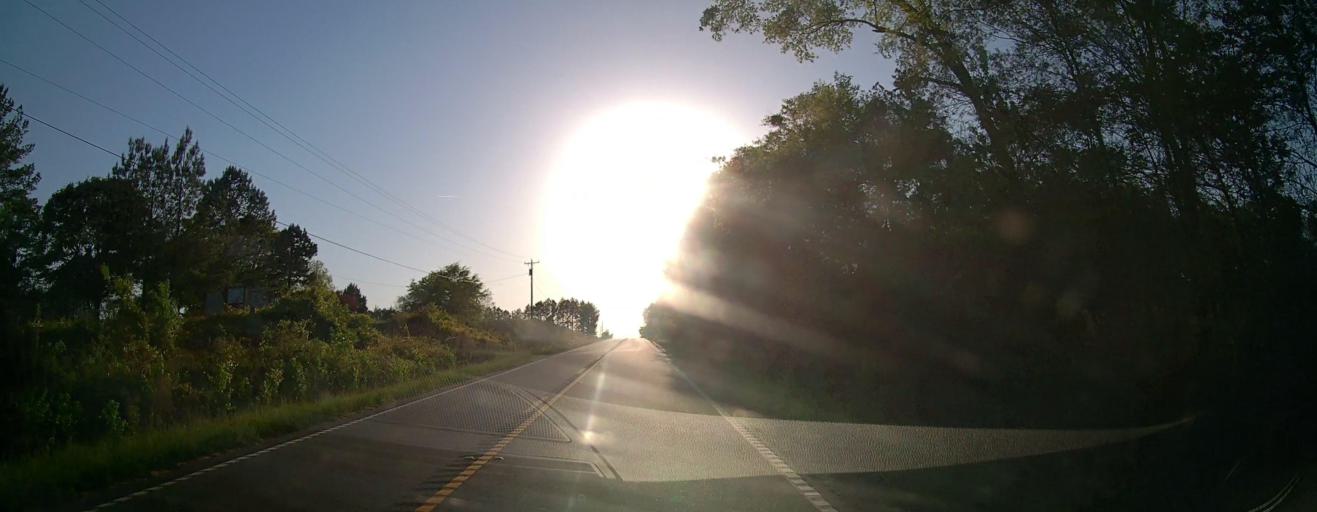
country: US
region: Georgia
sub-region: Schley County
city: Ellaville
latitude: 32.3208
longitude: -84.2888
